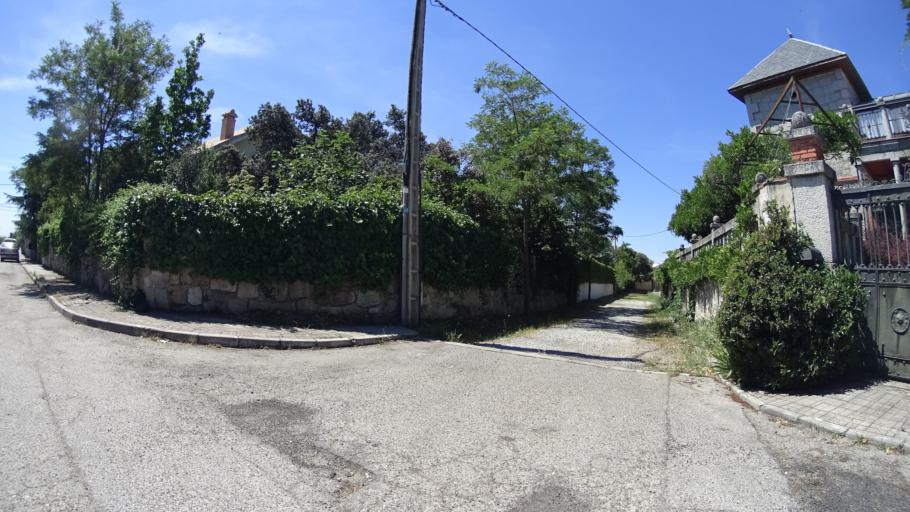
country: ES
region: Madrid
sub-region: Provincia de Madrid
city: Hoyo de Manzanares
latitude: 40.6258
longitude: -3.9038
